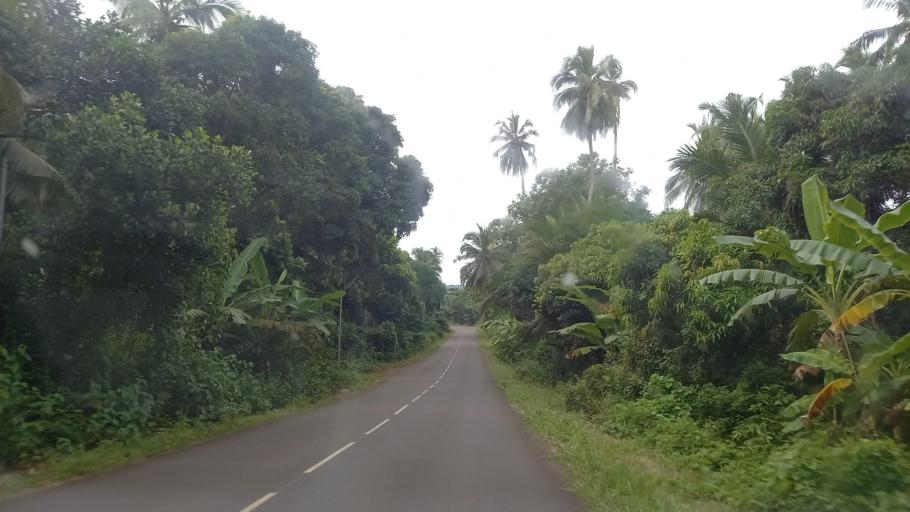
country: YT
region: Boueni
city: Boueni
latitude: -12.9184
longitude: 45.1017
